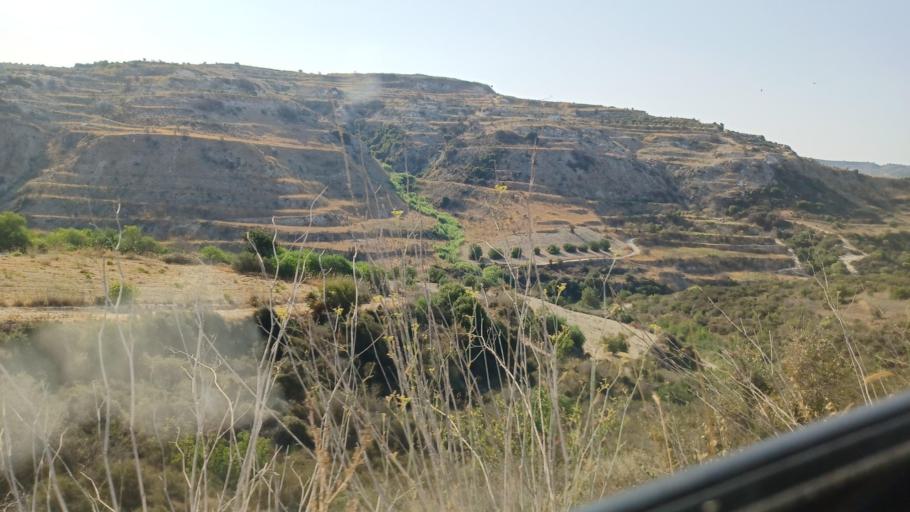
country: CY
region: Pafos
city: Tala
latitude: 34.8902
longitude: 32.4515
